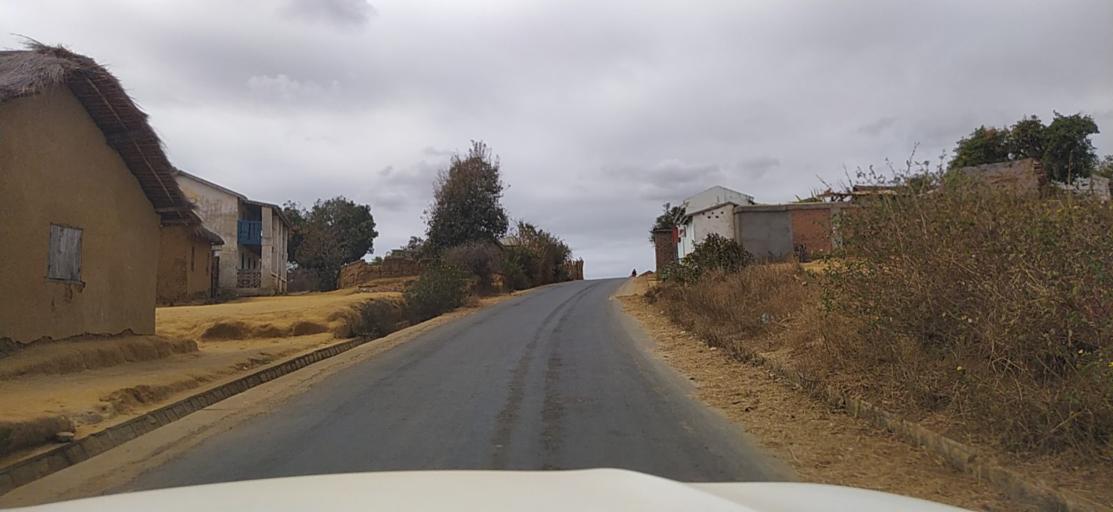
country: MG
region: Alaotra Mangoro
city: Ambatondrazaka
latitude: -17.9296
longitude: 48.2565
